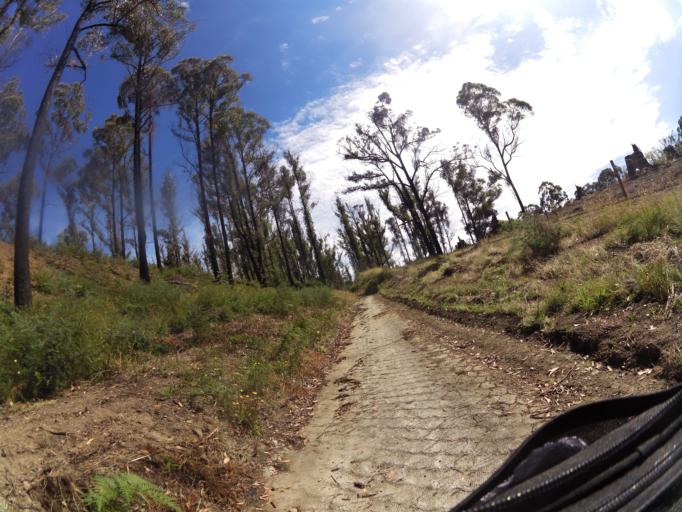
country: AU
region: Victoria
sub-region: East Gippsland
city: Lakes Entrance
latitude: -37.7315
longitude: 148.1624
